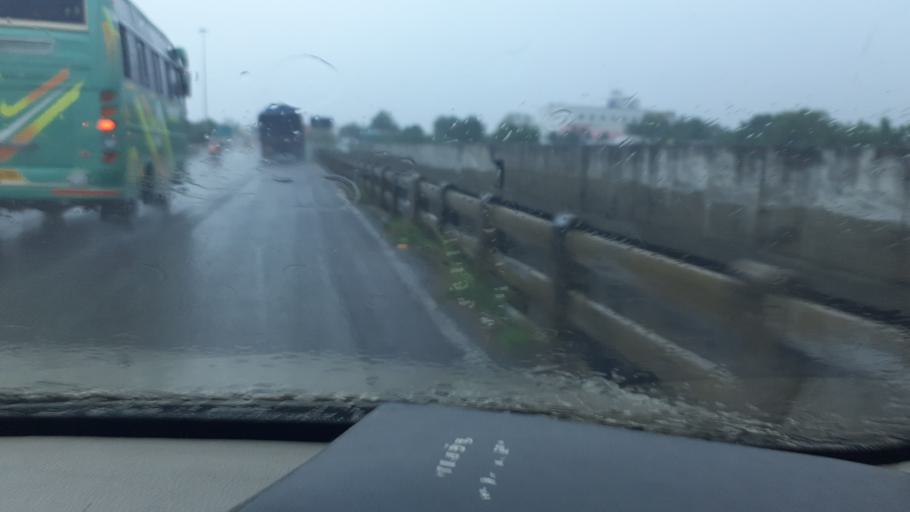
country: IN
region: Tamil Nadu
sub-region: Virudhunagar
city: Sattur
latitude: 9.3762
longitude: 77.9123
